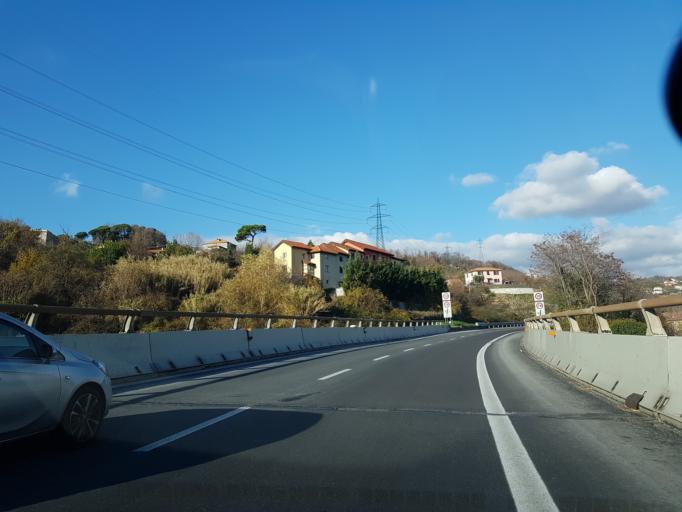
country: IT
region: Liguria
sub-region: Provincia di Genova
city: Pedemonte
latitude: 44.4962
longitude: 8.9162
